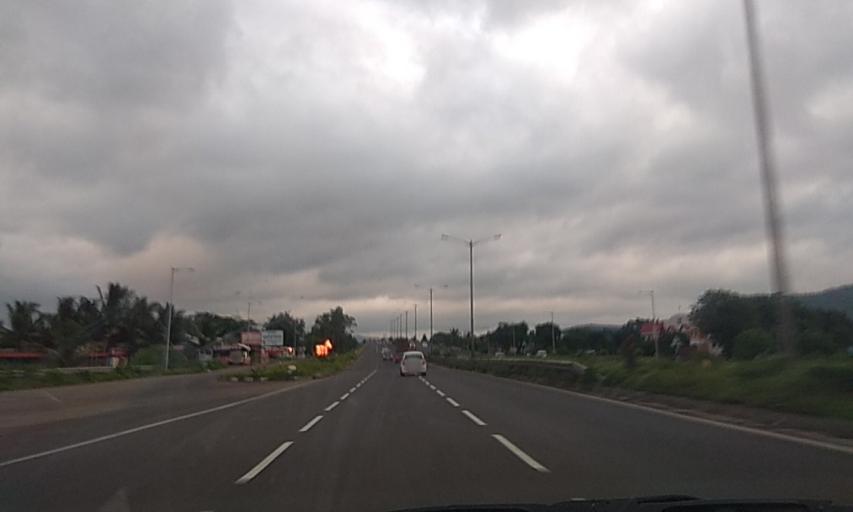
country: IN
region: Maharashtra
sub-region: Satara Division
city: Wai
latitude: 17.8998
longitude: 73.9717
